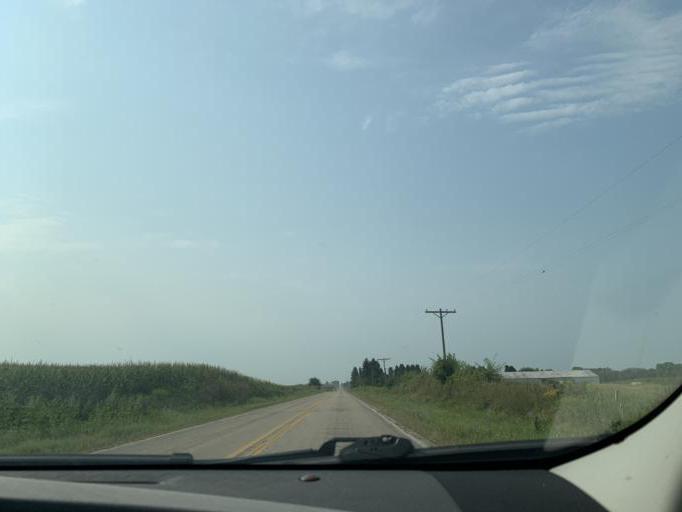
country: US
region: Illinois
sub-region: Whiteside County
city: Morrison
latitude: 41.8761
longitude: -89.9203
